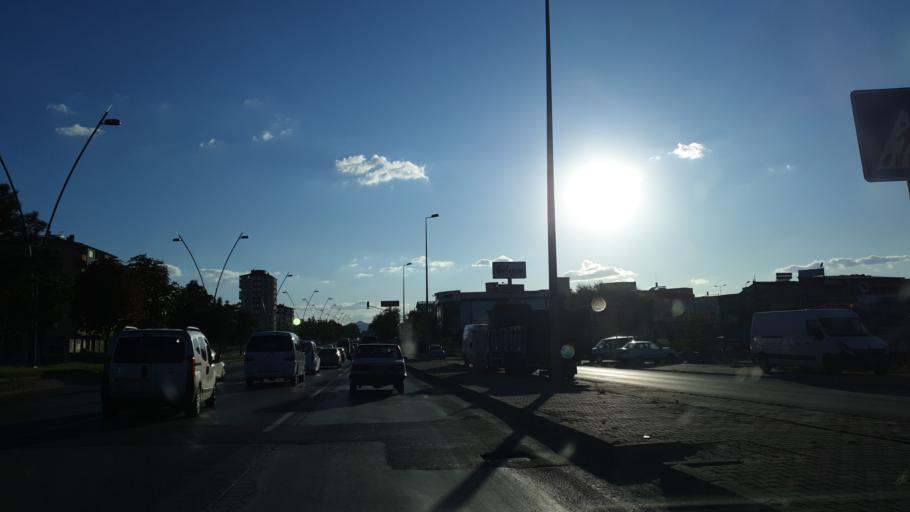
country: TR
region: Kayseri
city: Kocasinan
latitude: 38.7476
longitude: 35.5372
